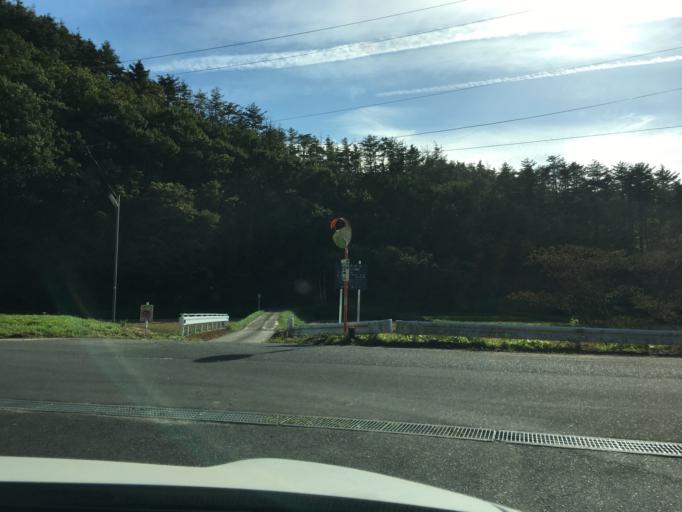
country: JP
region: Fukushima
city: Miharu
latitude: 37.3380
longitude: 140.4822
